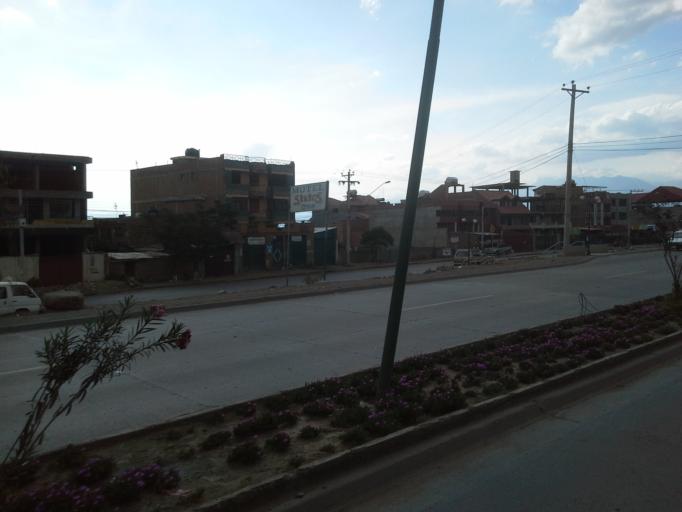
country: BO
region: Cochabamba
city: Cochabamba
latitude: -17.4310
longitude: -66.1505
